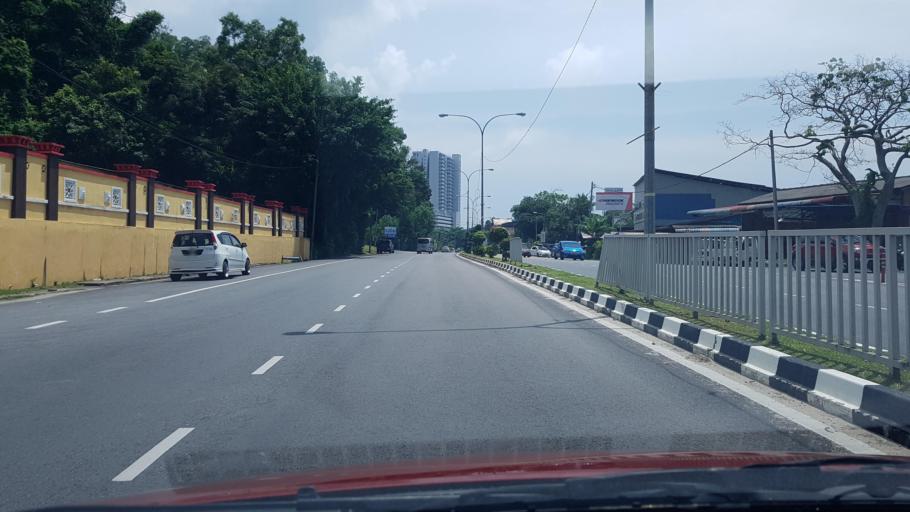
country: MY
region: Terengganu
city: Kuala Terengganu
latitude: 5.3165
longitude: 103.1446
